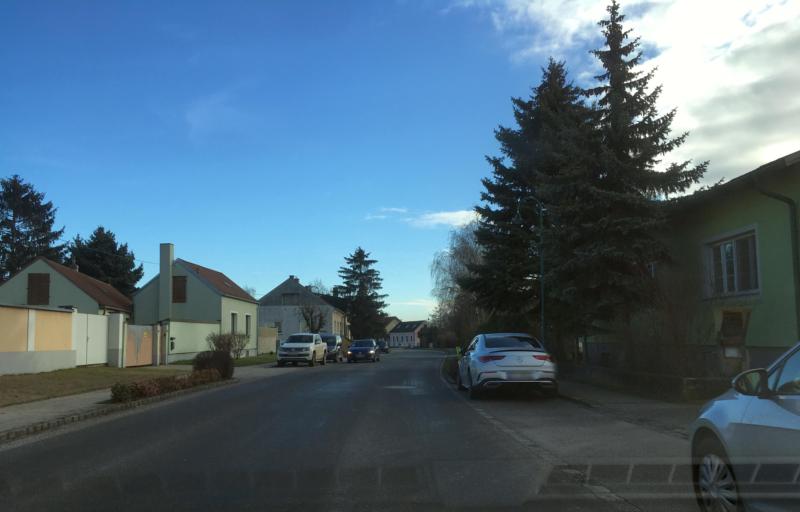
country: AT
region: Lower Austria
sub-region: Politischer Bezirk Ganserndorf
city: Eckartsau
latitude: 48.1447
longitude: 16.7993
